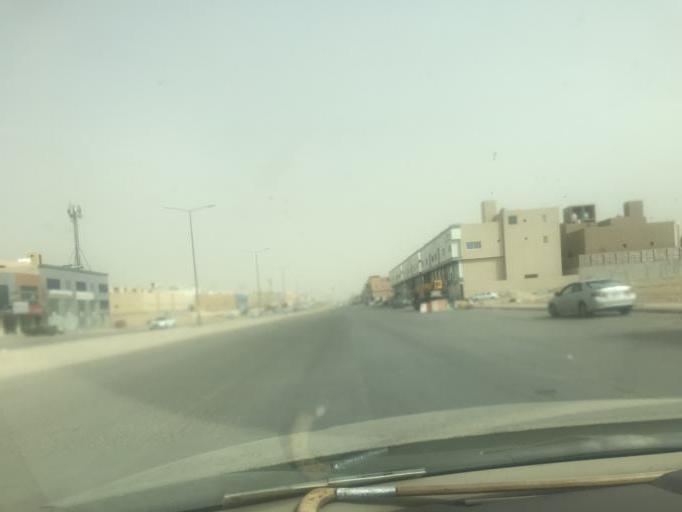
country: SA
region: Ar Riyad
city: Riyadh
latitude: 24.8040
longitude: 46.6039
